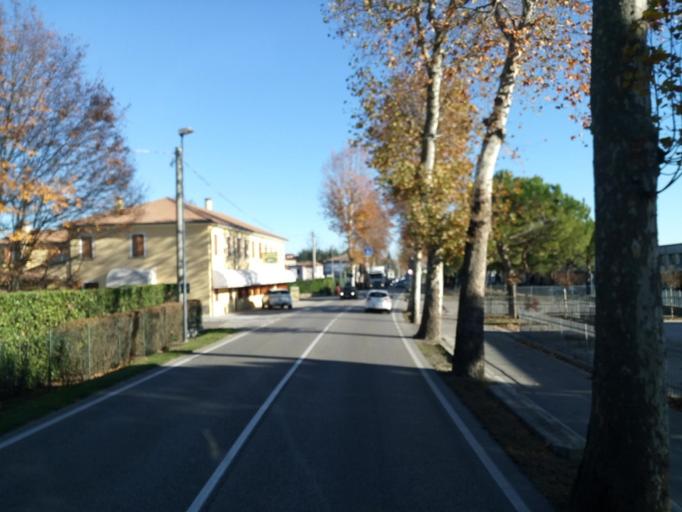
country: IT
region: Veneto
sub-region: Provincia di Treviso
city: Volpago del Montello
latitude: 45.7775
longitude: 12.1101
